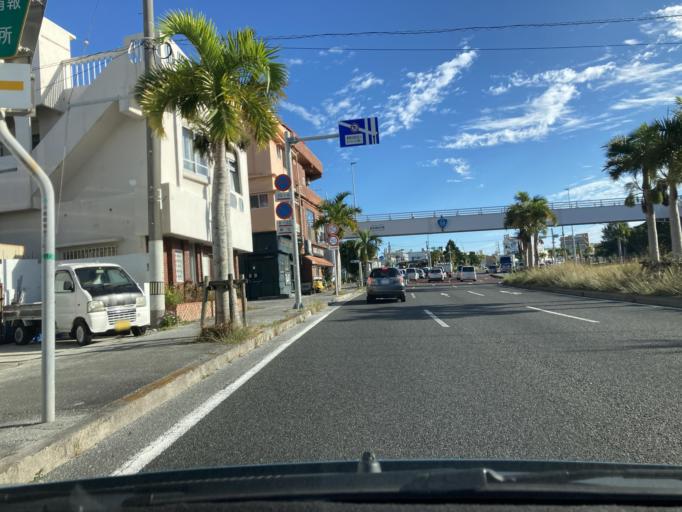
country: JP
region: Okinawa
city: Chatan
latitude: 26.3583
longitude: 127.7471
